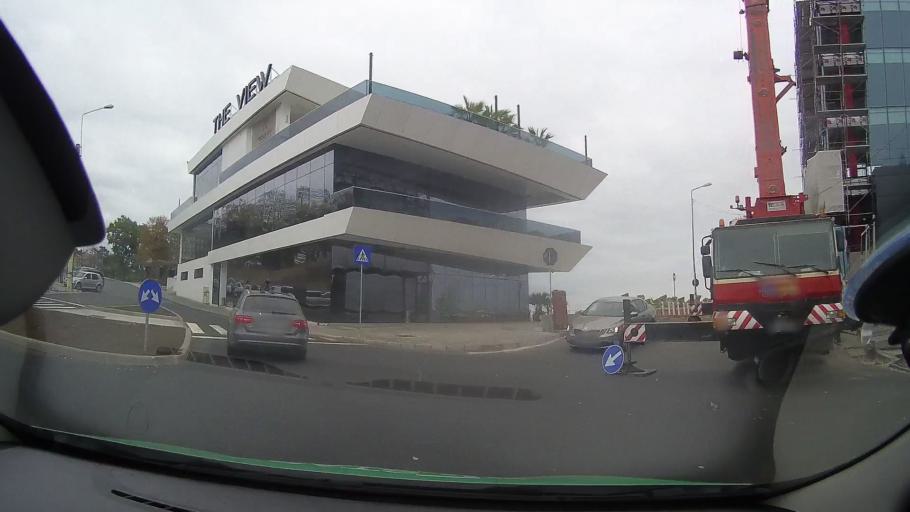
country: RO
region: Constanta
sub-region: Municipiul Constanta
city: Constanta
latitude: 44.1702
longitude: 28.6598
